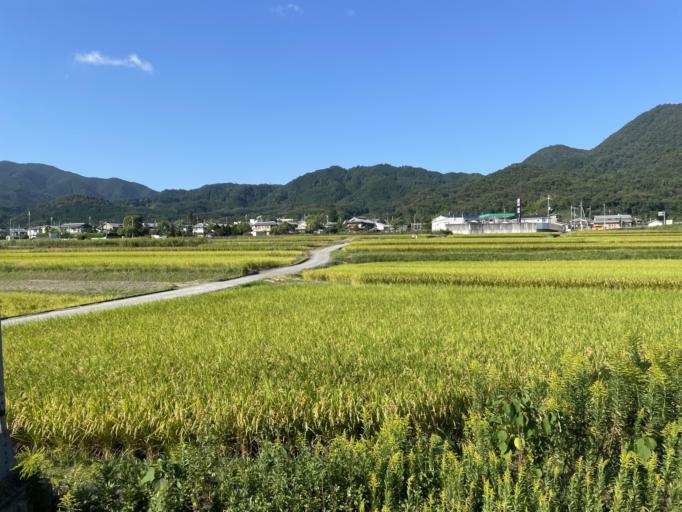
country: JP
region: Nara
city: Gose
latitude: 34.5251
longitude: 135.6994
